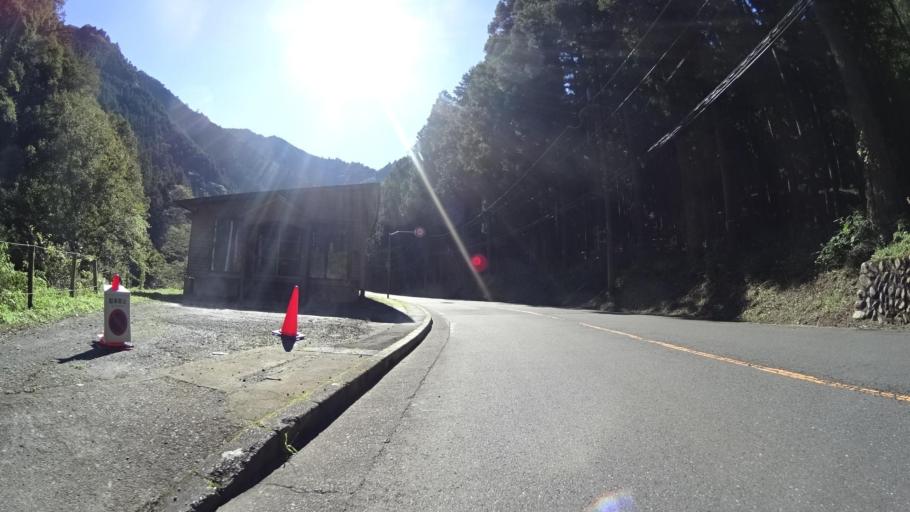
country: JP
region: Tokyo
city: Itsukaichi
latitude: 35.7183
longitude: 139.1500
